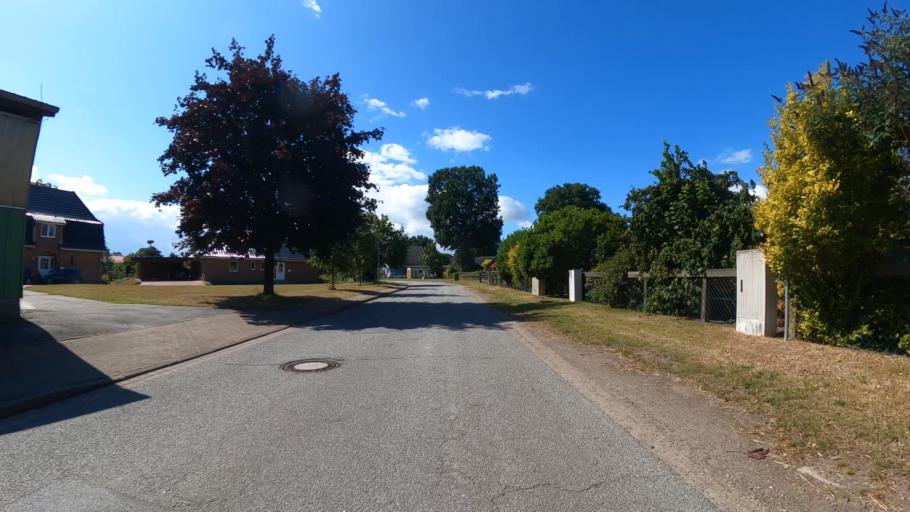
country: DE
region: Schleswig-Holstein
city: Armstedt
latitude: 53.9740
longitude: 9.8500
